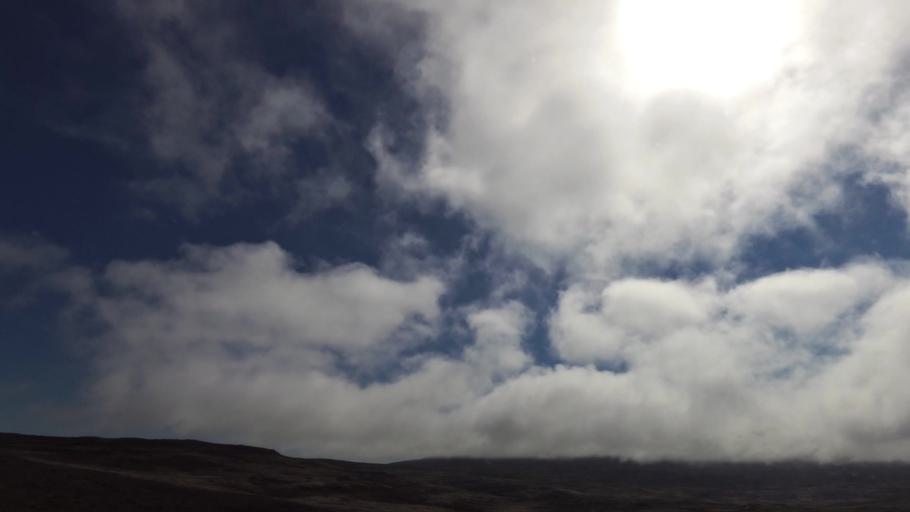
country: IS
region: West
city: Olafsvik
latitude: 65.5552
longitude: -24.2595
